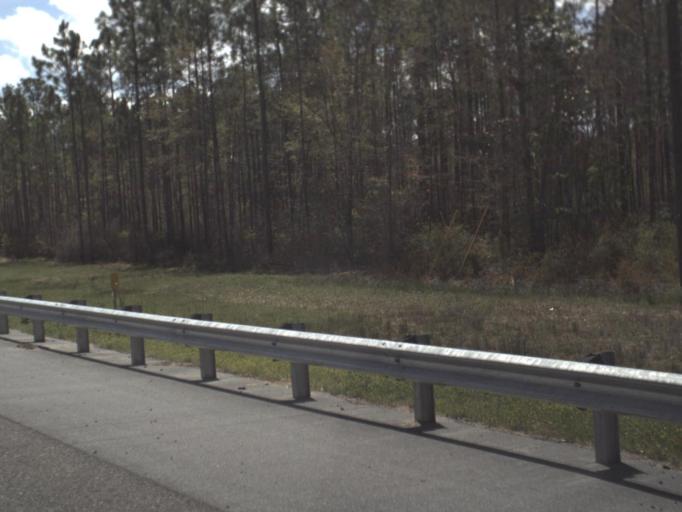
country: US
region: Florida
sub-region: Bay County
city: Laguna Beach
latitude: 30.4163
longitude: -85.8694
